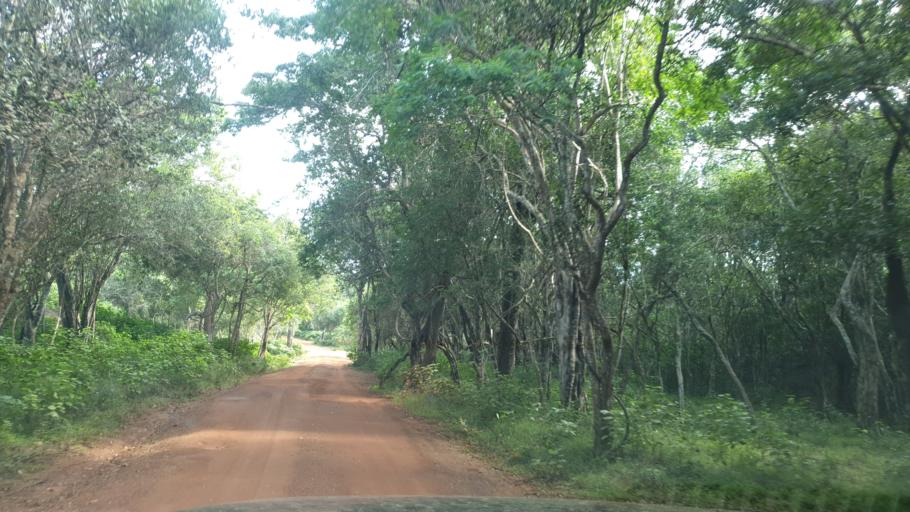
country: LK
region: North Central
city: Anuradhapura
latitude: 8.3837
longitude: 80.0612
